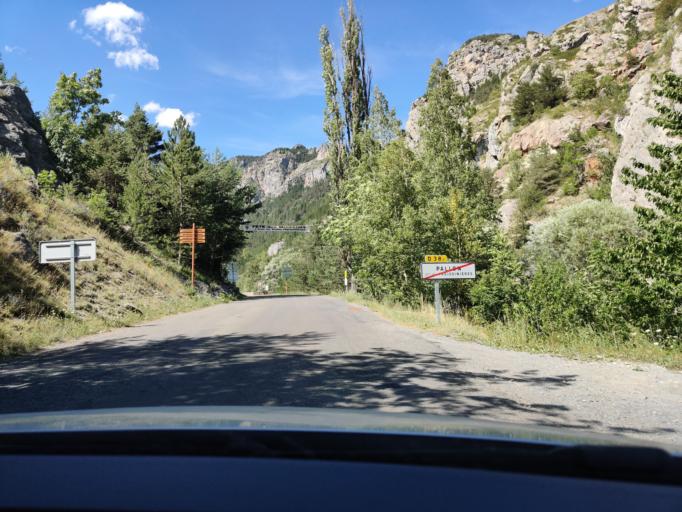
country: FR
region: Provence-Alpes-Cote d'Azur
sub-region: Departement des Hautes-Alpes
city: Saint-Martin-de-Queyrieres
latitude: 44.7390
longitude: 6.5642
